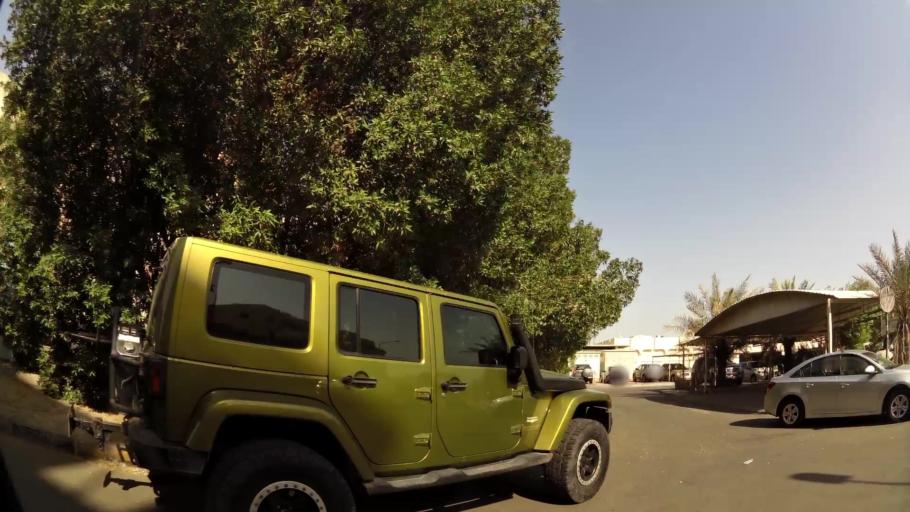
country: KW
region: Muhafazat Hawalli
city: Salwa
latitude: 29.2867
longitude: 48.0756
